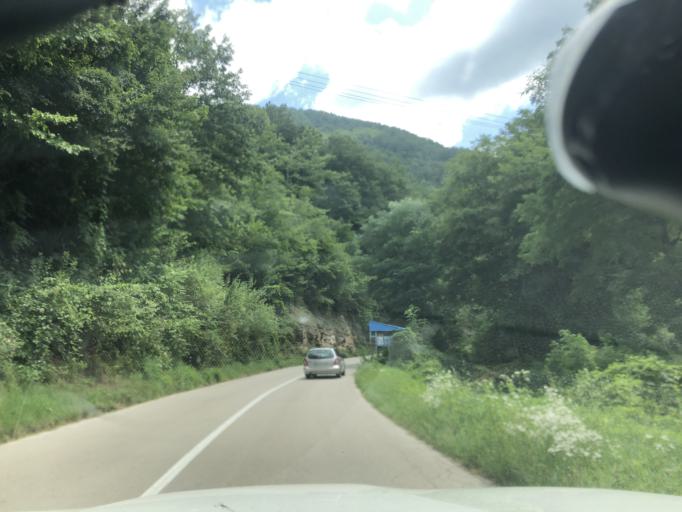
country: RS
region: Central Serbia
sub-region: Jablanicki Okrug
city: Medvega
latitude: 42.7881
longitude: 21.5848
